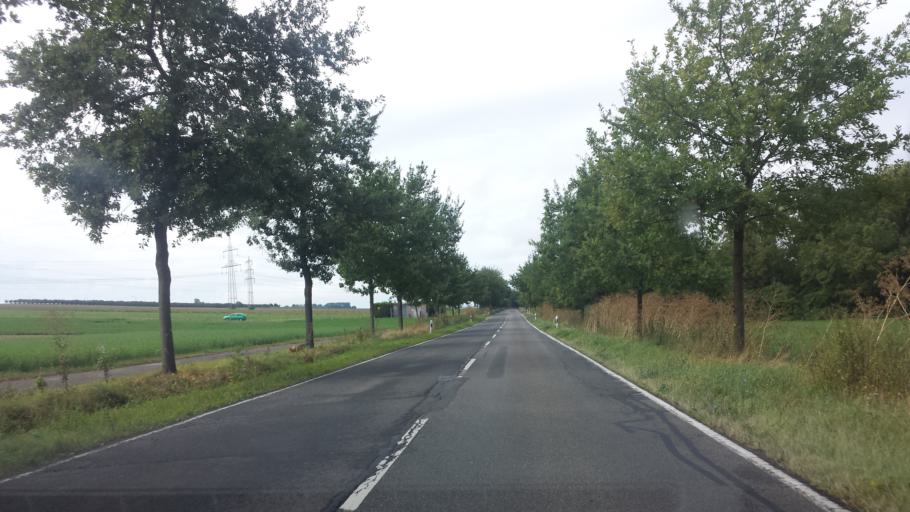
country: DE
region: Rheinland-Pfalz
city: Bechtheim
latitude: 49.7035
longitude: 8.2893
